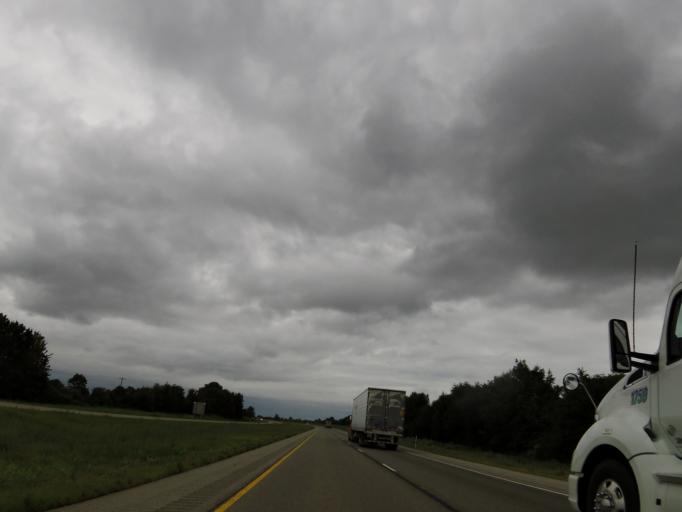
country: US
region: Illinois
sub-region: Massac County
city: Metropolis
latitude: 37.1788
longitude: -88.6823
